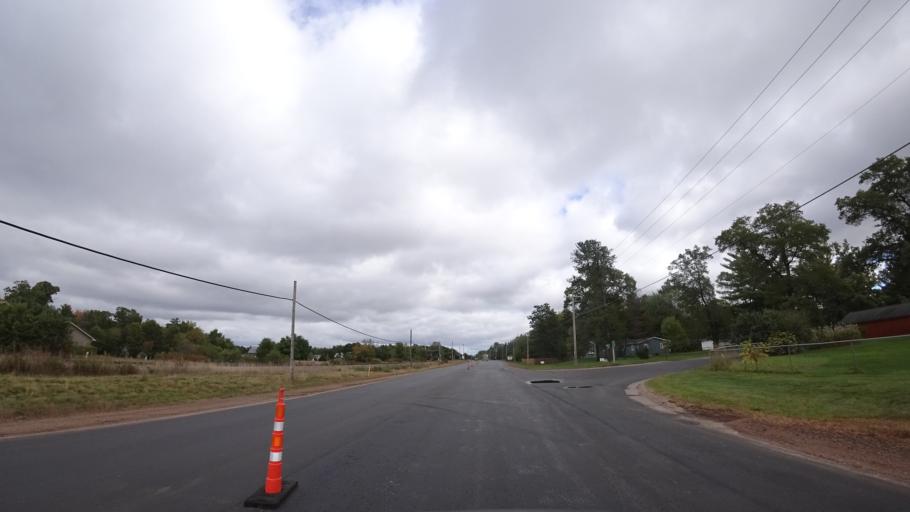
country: US
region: Wisconsin
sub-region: Chippewa County
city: Lake Wissota
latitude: 44.9282
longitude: -91.2902
